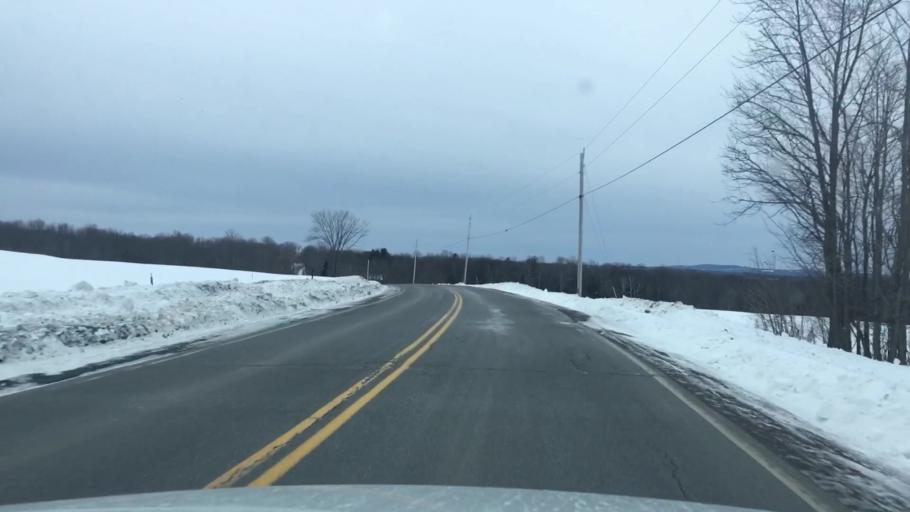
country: US
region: Maine
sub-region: Penobscot County
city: Corinna
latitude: 44.9452
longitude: -69.2150
